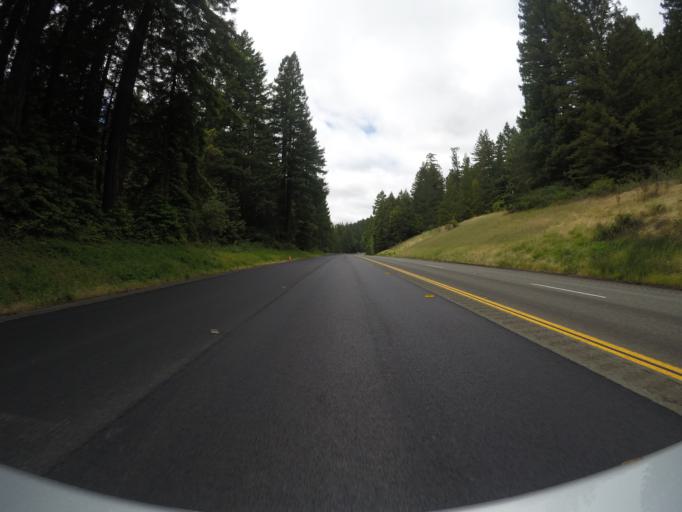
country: US
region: California
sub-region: Humboldt County
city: Redway
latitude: 40.3070
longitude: -123.9034
